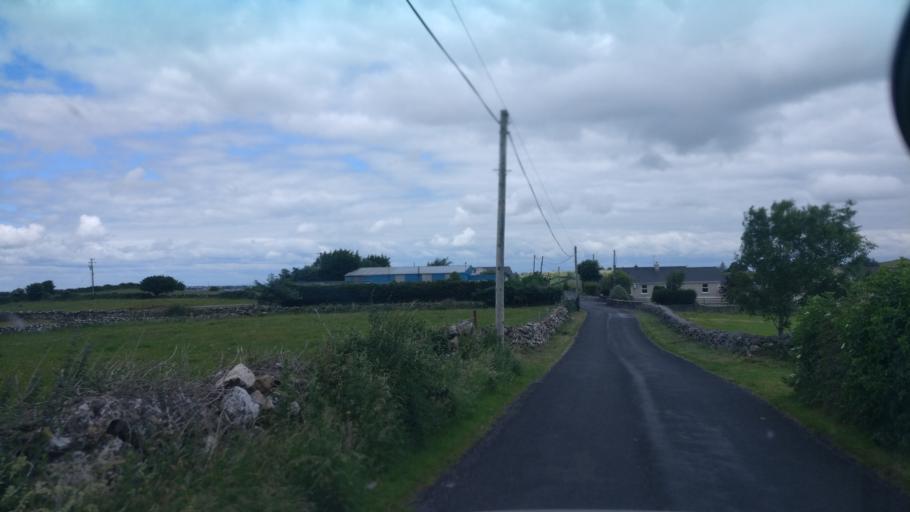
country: IE
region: Connaught
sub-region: County Galway
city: Loughrea
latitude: 53.1727
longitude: -8.5557
